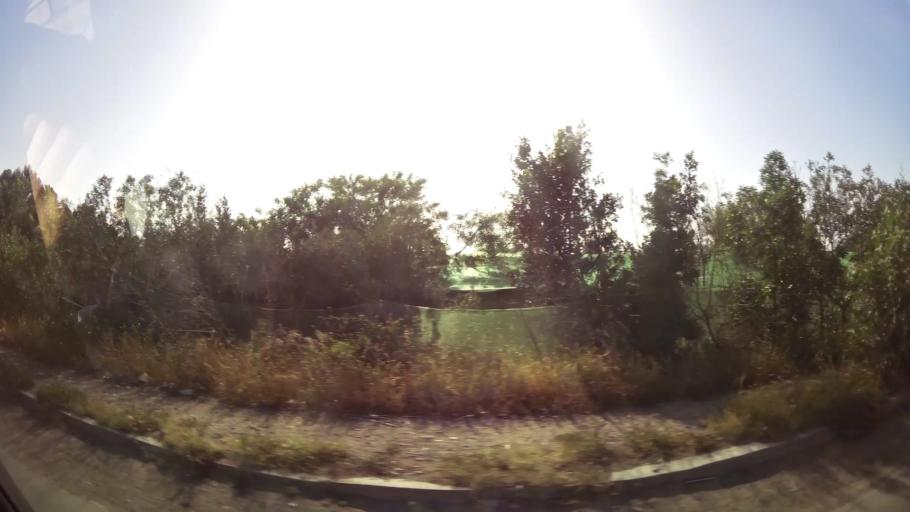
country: MA
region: Souss-Massa-Draa
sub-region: Inezgane-Ait Mellou
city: Inezgane
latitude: 30.3599
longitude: -9.5060
